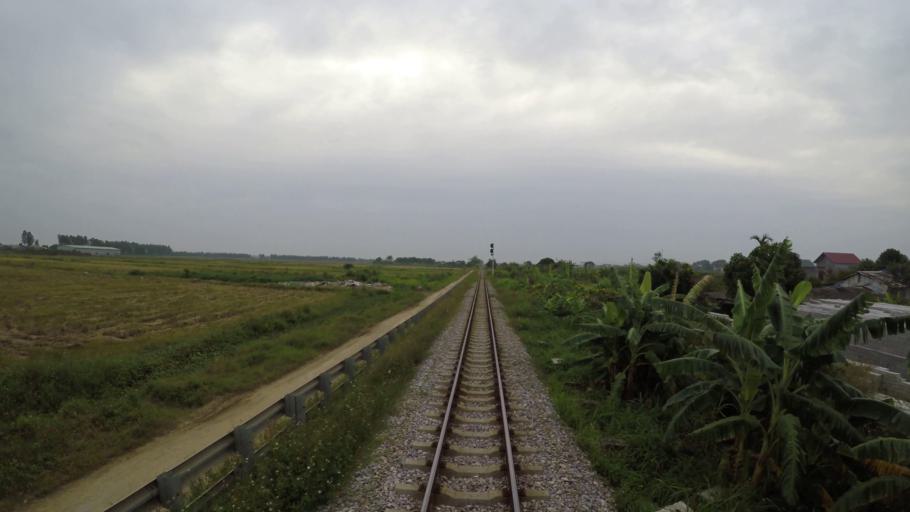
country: VN
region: Bac Ninh
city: Thua
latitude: 20.9665
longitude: 106.1723
